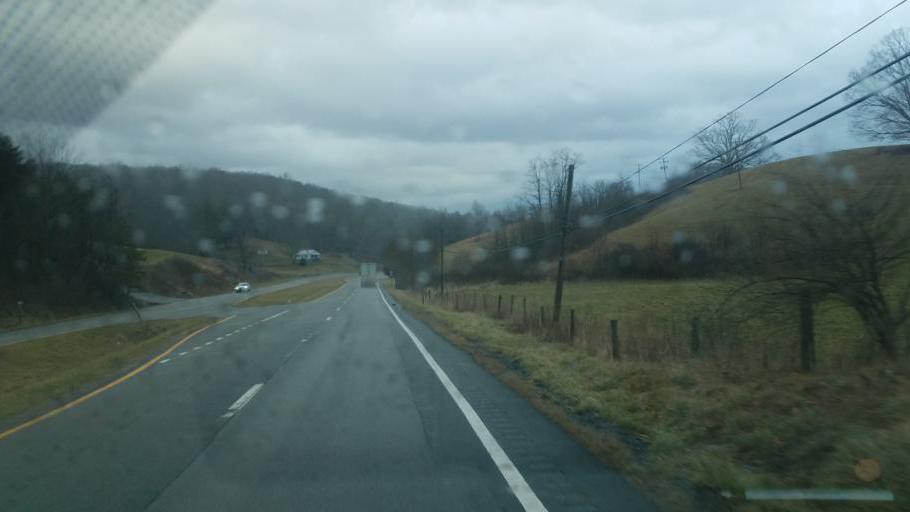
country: US
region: Virginia
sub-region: Giles County
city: Pearisburg
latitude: 37.2832
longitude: -80.7439
